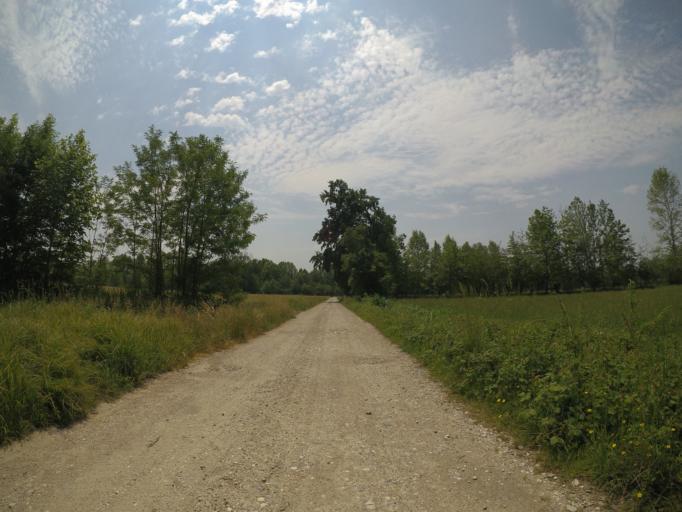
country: IT
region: Friuli Venezia Giulia
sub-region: Provincia di Udine
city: Bertiolo
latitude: 45.9206
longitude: 13.0390
